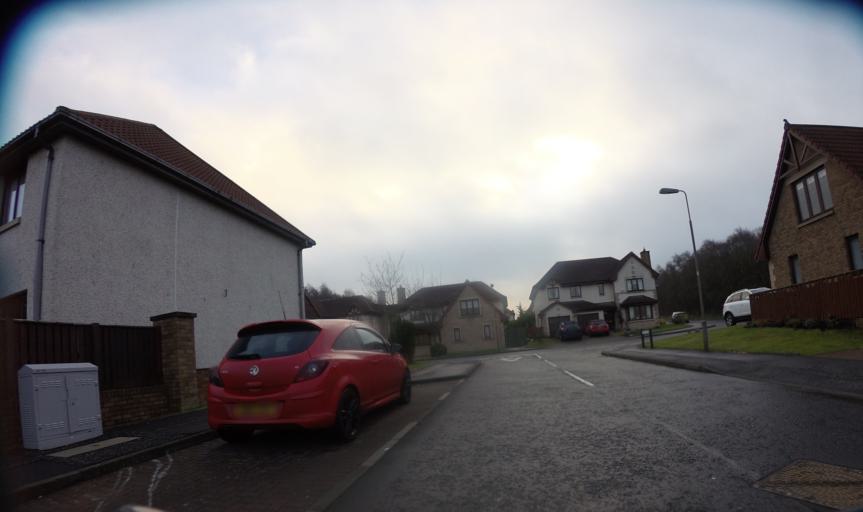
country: GB
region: Scotland
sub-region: West Lothian
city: Livingston
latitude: 55.8720
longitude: -3.5326
